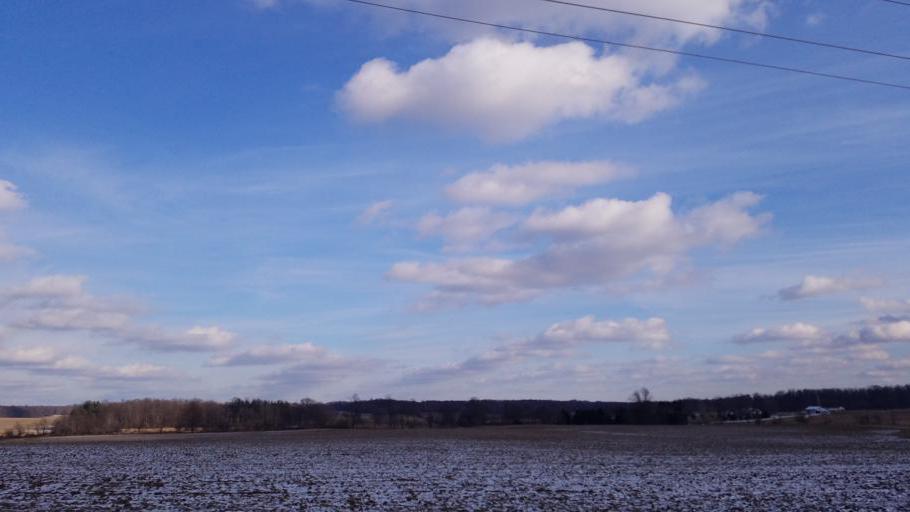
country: US
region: Ohio
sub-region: Crawford County
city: Galion
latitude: 40.6693
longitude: -82.7185
